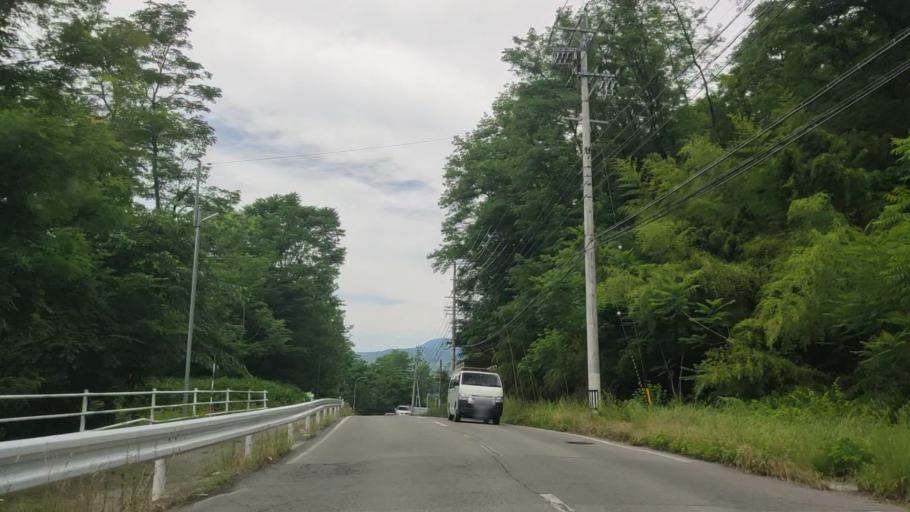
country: JP
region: Nagano
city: Kamimaruko
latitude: 36.3348
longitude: 138.3513
